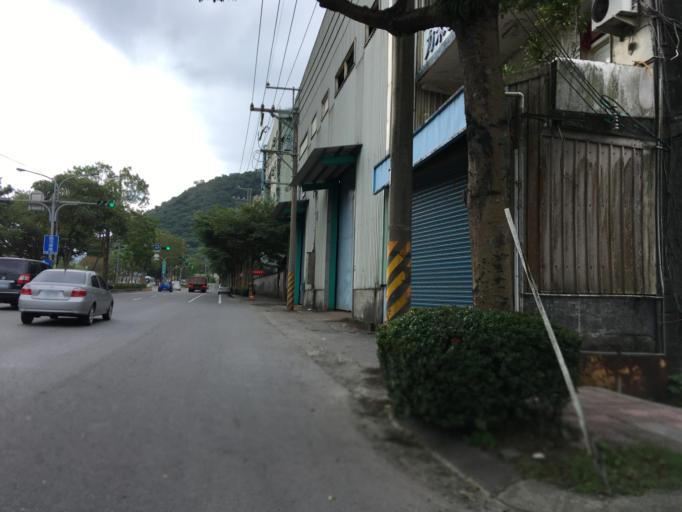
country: TW
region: Taiwan
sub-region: Yilan
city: Yilan
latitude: 24.6104
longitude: 121.8259
